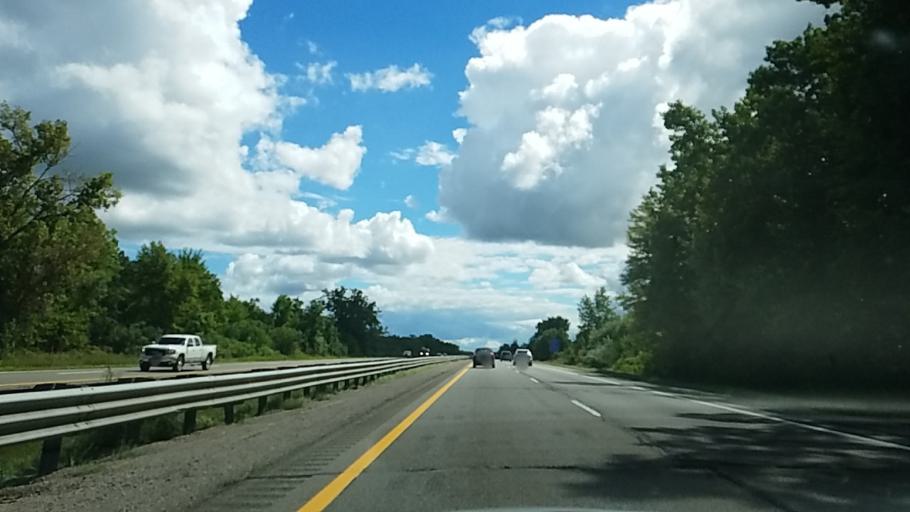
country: US
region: Michigan
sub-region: Washtenaw County
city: Ann Arbor
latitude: 42.3502
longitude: -83.7470
